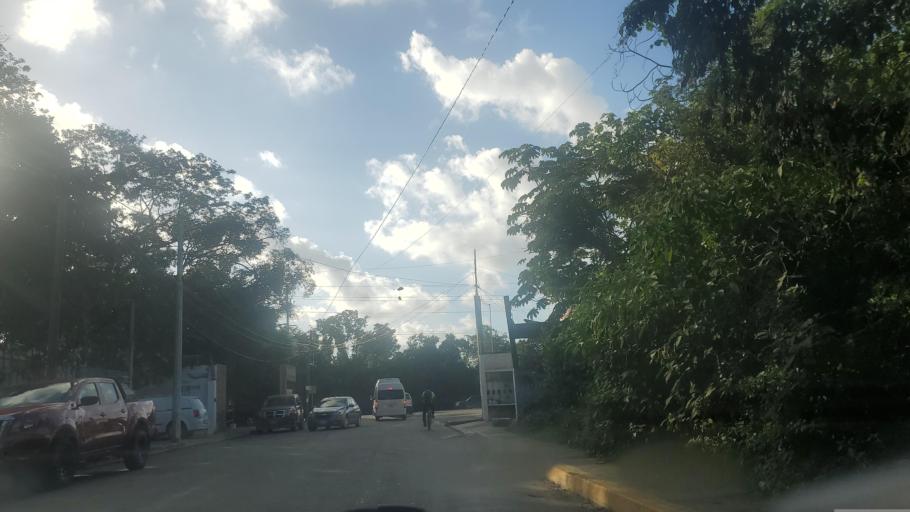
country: MX
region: Quintana Roo
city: Tulum
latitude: 20.2158
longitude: -87.4509
